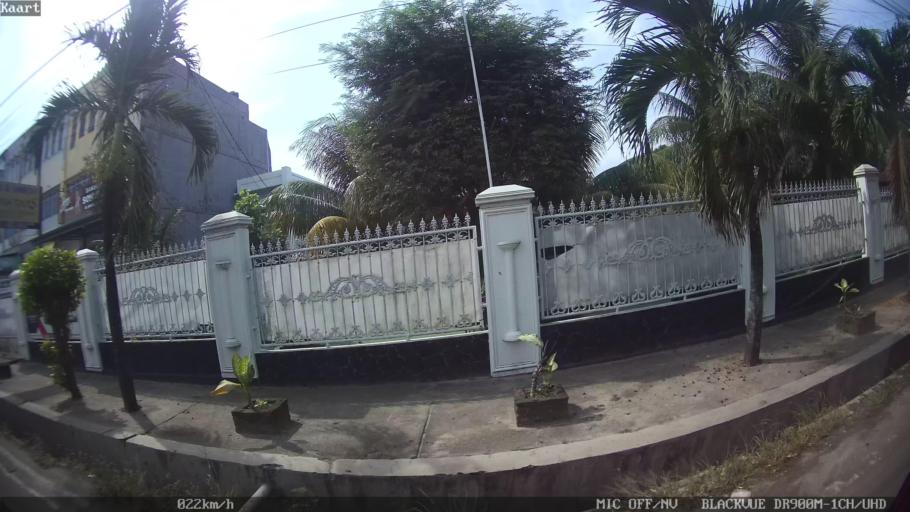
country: ID
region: Lampung
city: Kedaton
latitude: -5.3876
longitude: 105.2910
